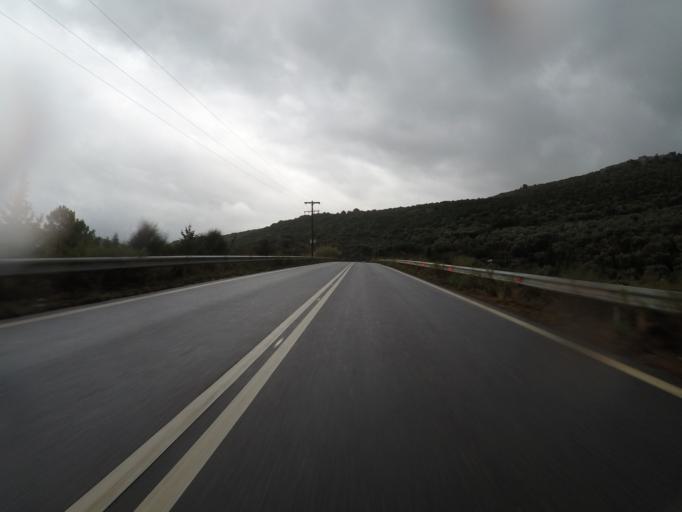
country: GR
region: Peloponnese
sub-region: Nomos Messinias
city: Pylos
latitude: 36.9316
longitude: 21.7274
